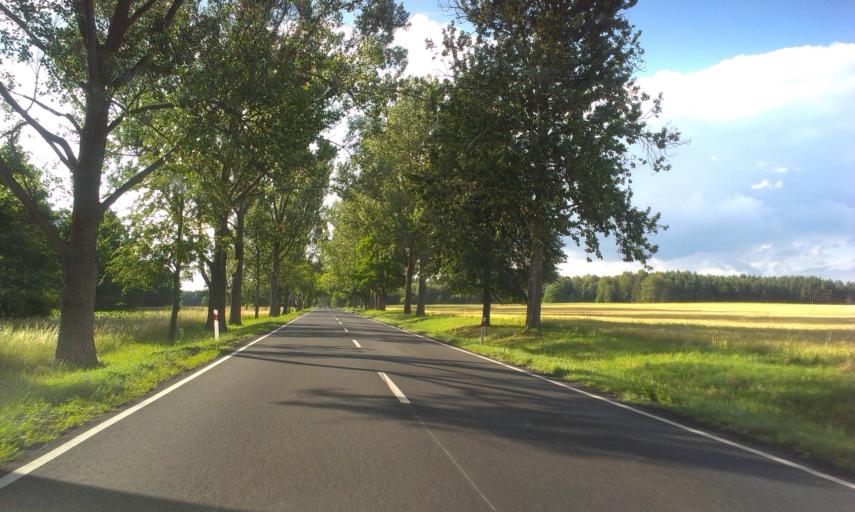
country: PL
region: Greater Poland Voivodeship
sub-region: Powiat zlotowski
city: Okonek
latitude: 53.4837
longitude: 16.8712
